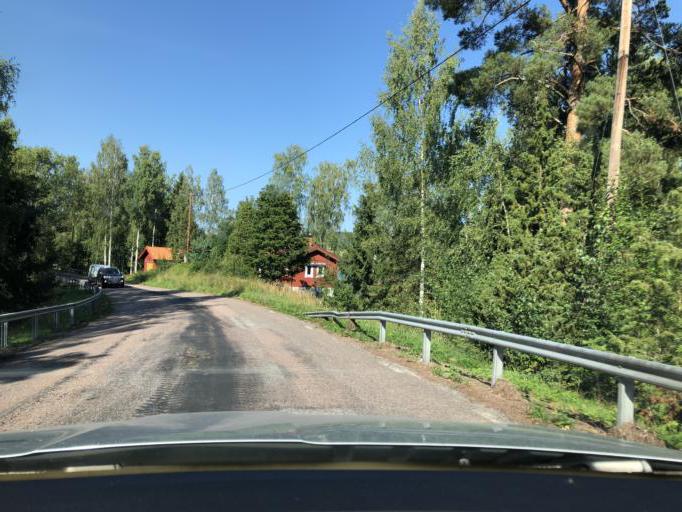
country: SE
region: Dalarna
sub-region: Hedemora Kommun
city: Hedemora
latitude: 60.3454
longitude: 15.9289
